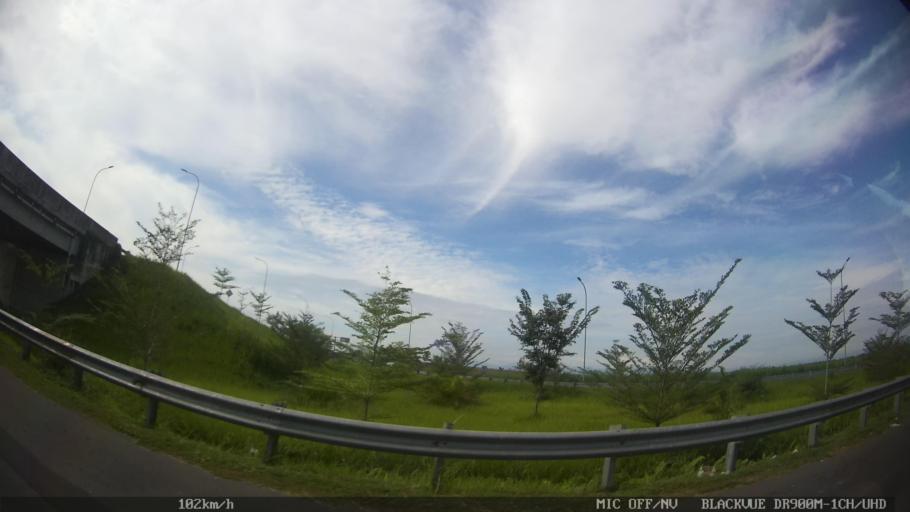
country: ID
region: North Sumatra
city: Sunggal
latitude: 3.6373
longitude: 98.5819
